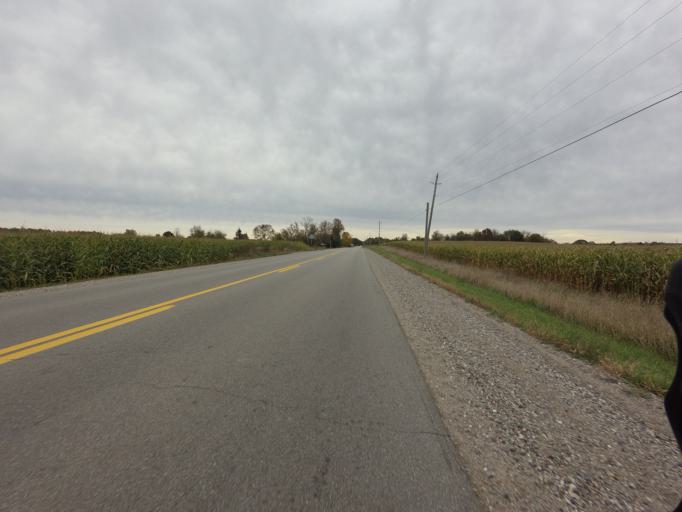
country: CA
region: Ontario
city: Gananoque
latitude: 44.5308
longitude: -76.1499
